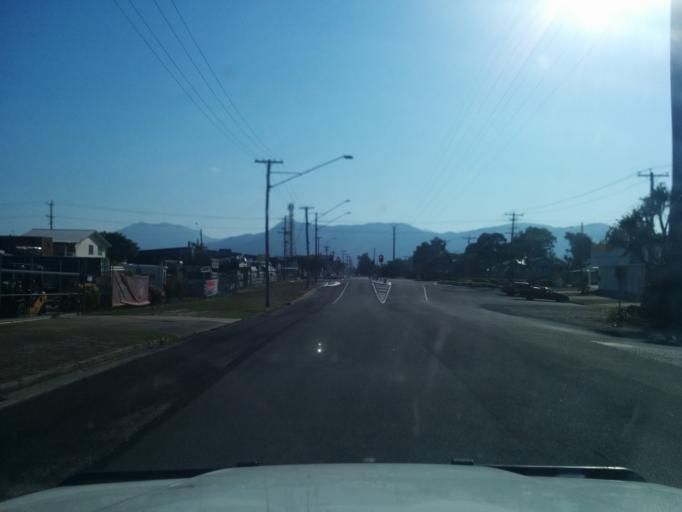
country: AU
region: Queensland
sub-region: Cairns
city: Cairns
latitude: -16.9351
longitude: 145.7673
